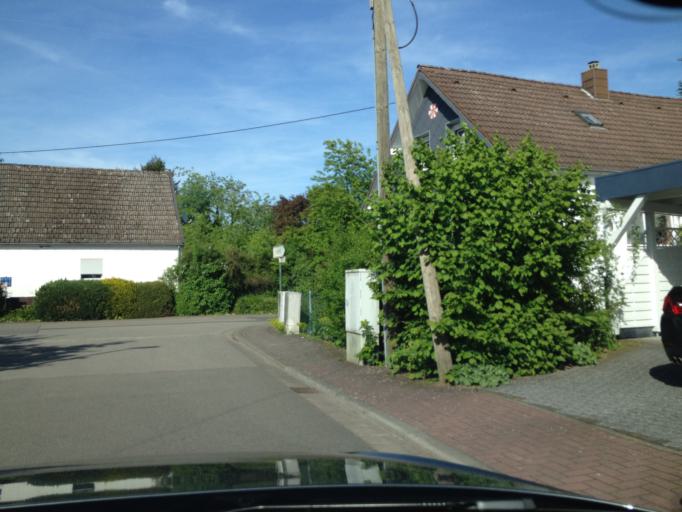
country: DE
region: Saarland
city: Bexbach
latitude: 49.3228
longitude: 7.2458
